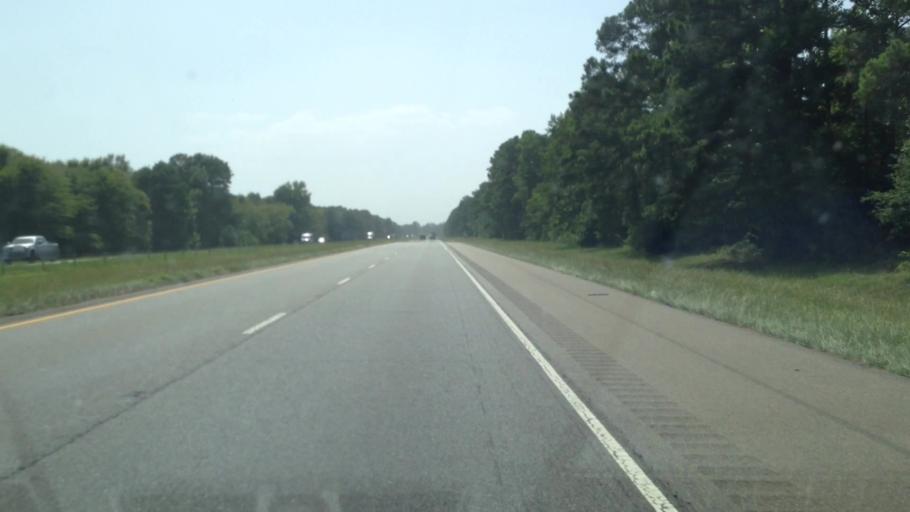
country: US
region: Louisiana
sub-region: Bossier Parish
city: Haughton
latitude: 32.5772
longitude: -93.4552
